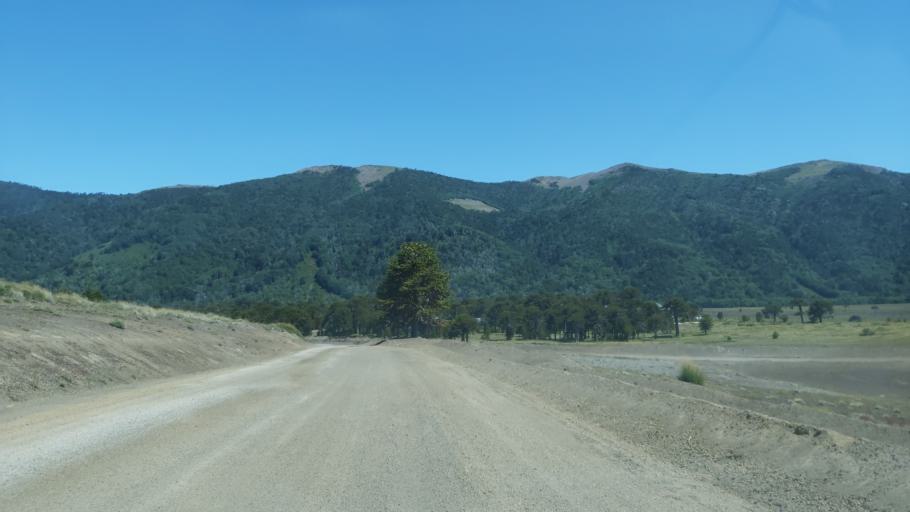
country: CL
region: Araucania
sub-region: Provincia de Cautin
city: Vilcun
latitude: -38.4162
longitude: -71.5430
